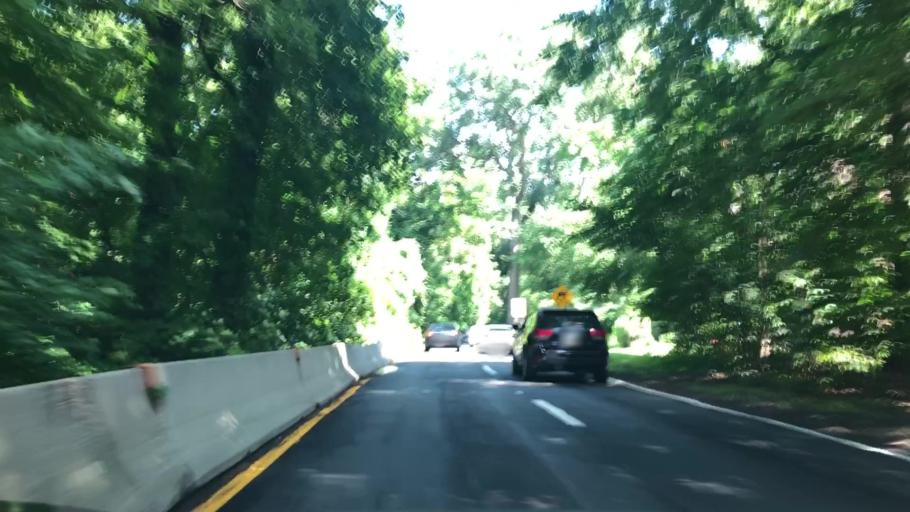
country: US
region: New York
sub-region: Westchester County
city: Greenville
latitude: 40.9813
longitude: -73.8138
